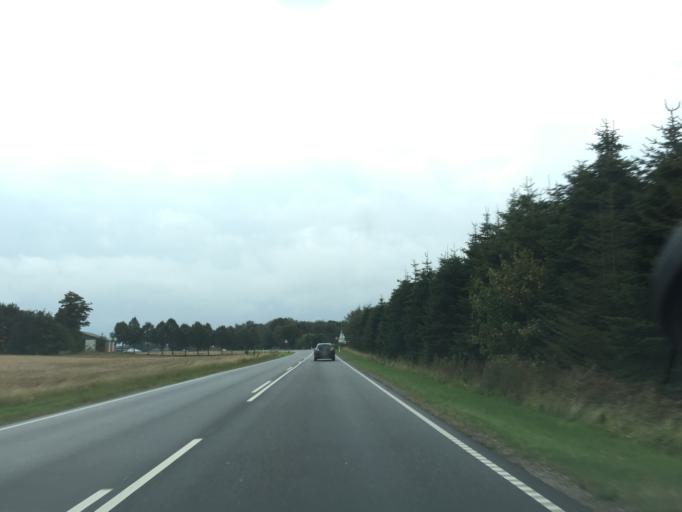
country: DK
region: Central Jutland
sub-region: Skanderborg Kommune
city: Skanderborg
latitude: 56.0722
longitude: 9.8957
